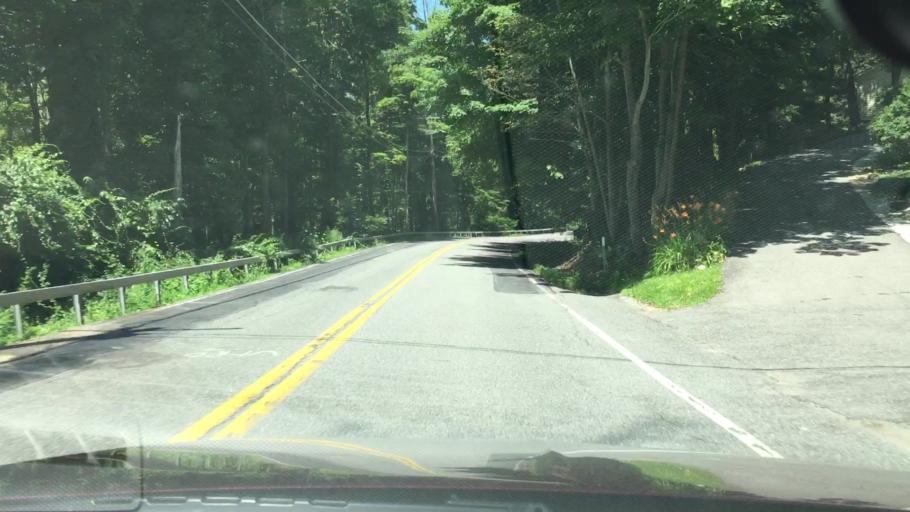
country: US
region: New York
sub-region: Putnam County
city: Lake Carmel
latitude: 41.4873
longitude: -73.6563
